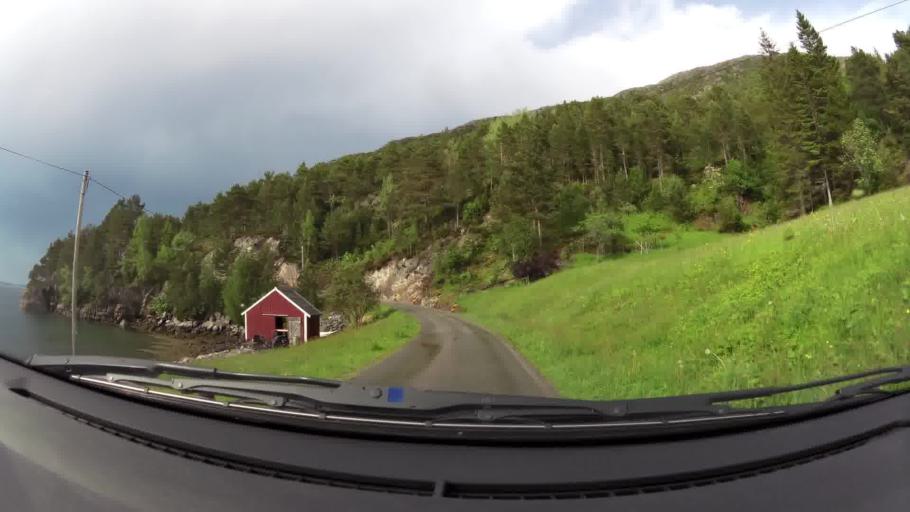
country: NO
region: More og Romsdal
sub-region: Kristiansund
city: Kristiansund
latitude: 63.0528
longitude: 7.7265
